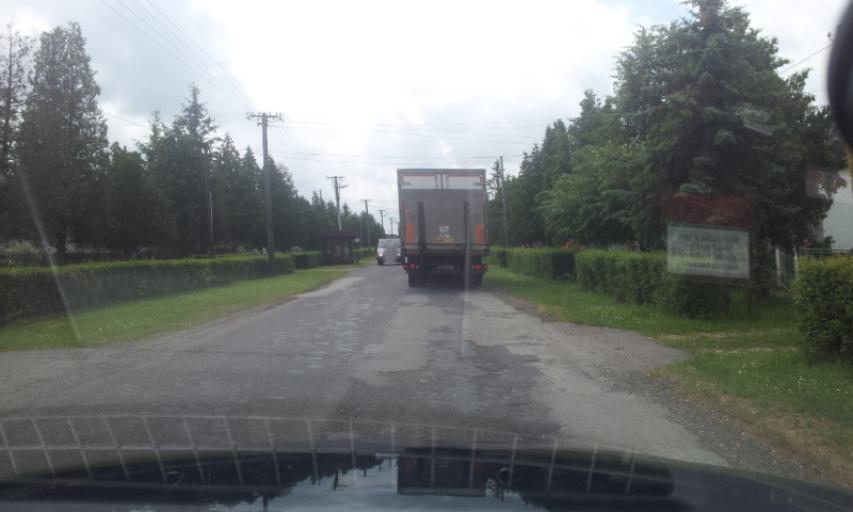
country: SK
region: Kosicky
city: Michalovce
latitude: 48.6229
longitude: 21.9874
